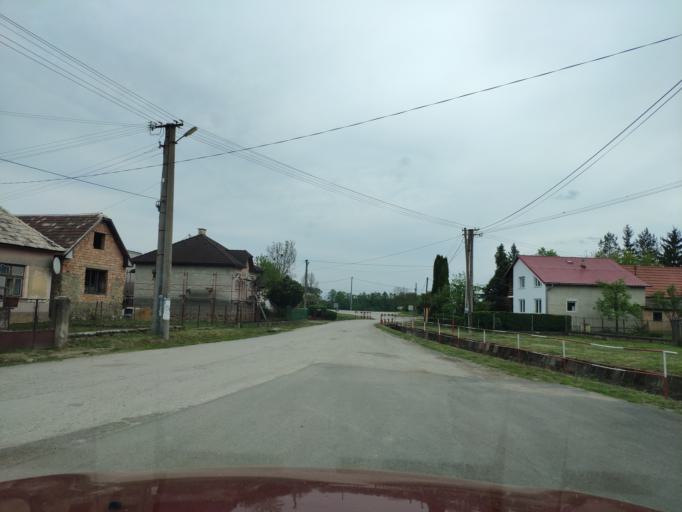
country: SK
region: Banskobystricky
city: Revuca
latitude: 48.5125
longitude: 20.1773
